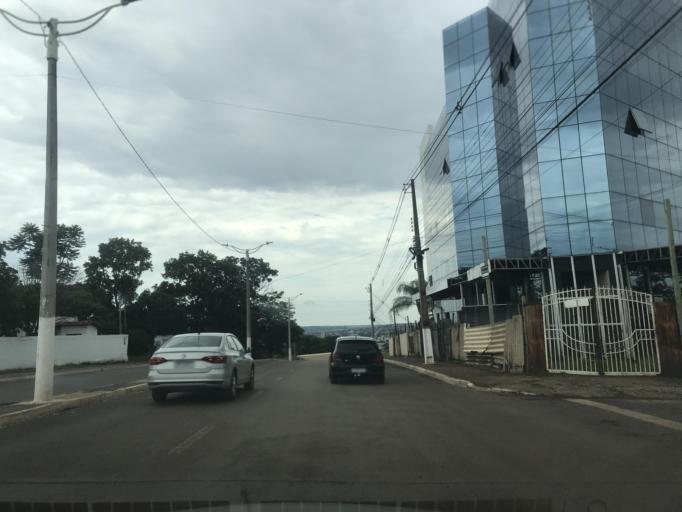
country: BR
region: Goias
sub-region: Luziania
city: Luziania
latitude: -16.2398
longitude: -47.9433
